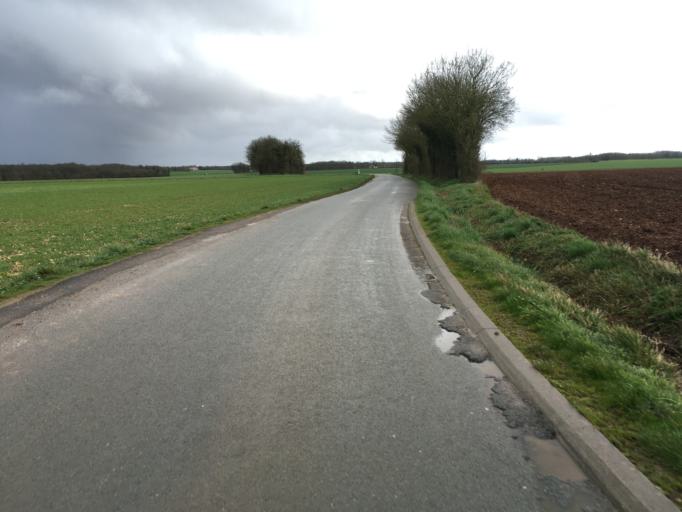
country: FR
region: Poitou-Charentes
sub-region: Departement de la Charente-Maritime
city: Surgeres
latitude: 46.1337
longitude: -0.7760
